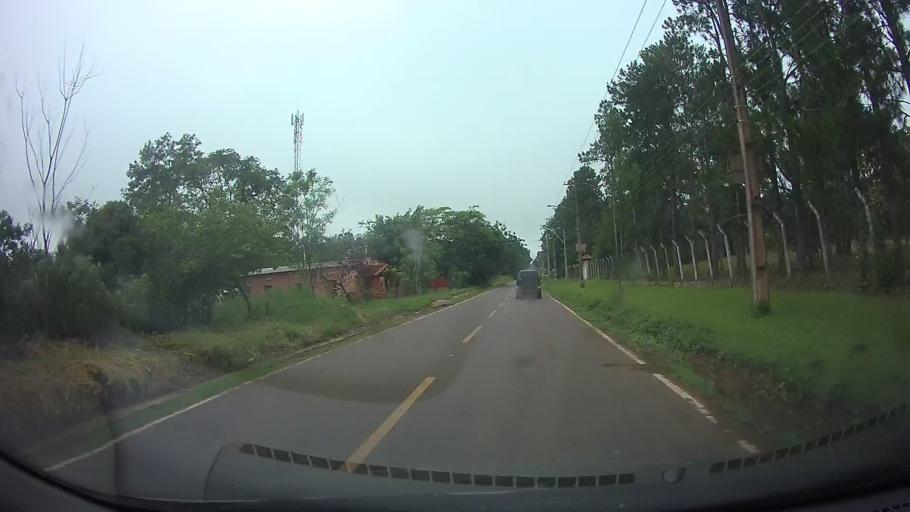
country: PY
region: Central
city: Itaugua
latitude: -25.3641
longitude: -57.3462
